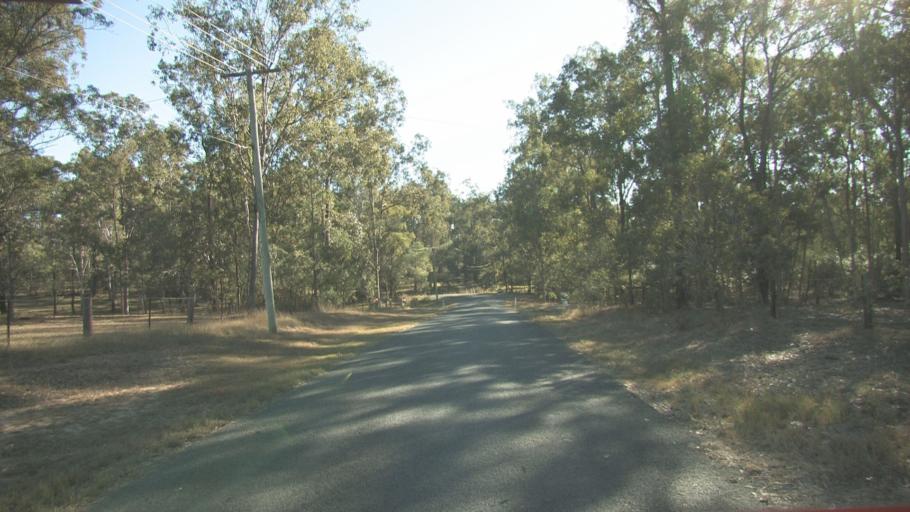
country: AU
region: Queensland
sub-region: Logan
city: North Maclean
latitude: -27.7809
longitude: 152.9653
